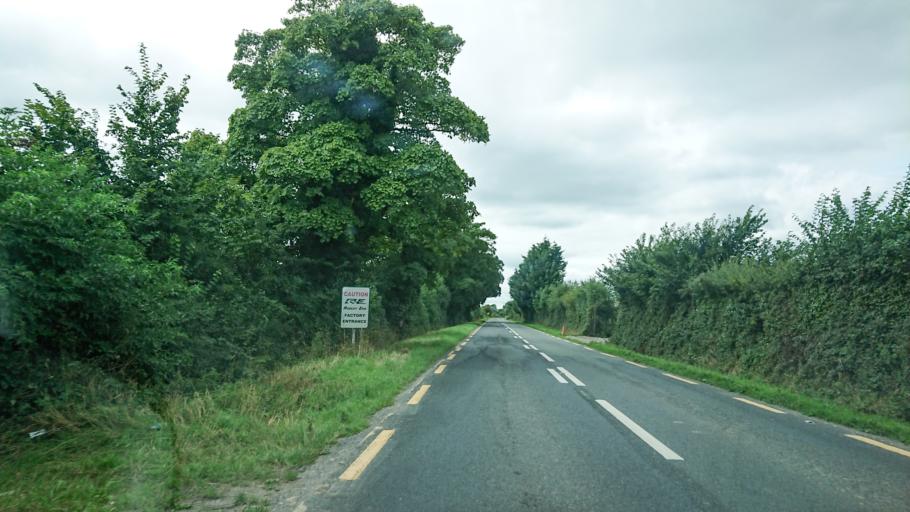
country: IE
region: Munster
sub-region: Waterford
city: Dungarvan
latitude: 52.1076
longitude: -7.6513
